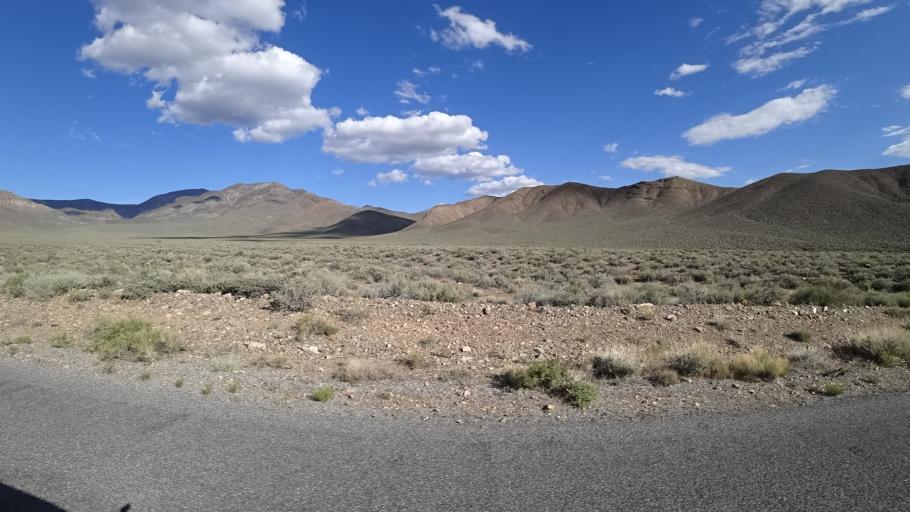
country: US
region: California
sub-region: San Bernardino County
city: Searles Valley
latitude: 36.3030
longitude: -117.1642
